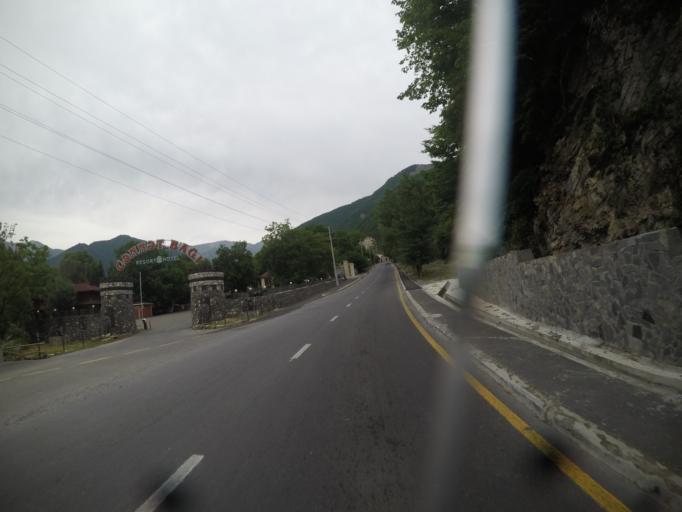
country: AZ
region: Shaki City
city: Sheki
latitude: 41.2438
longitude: 47.1973
